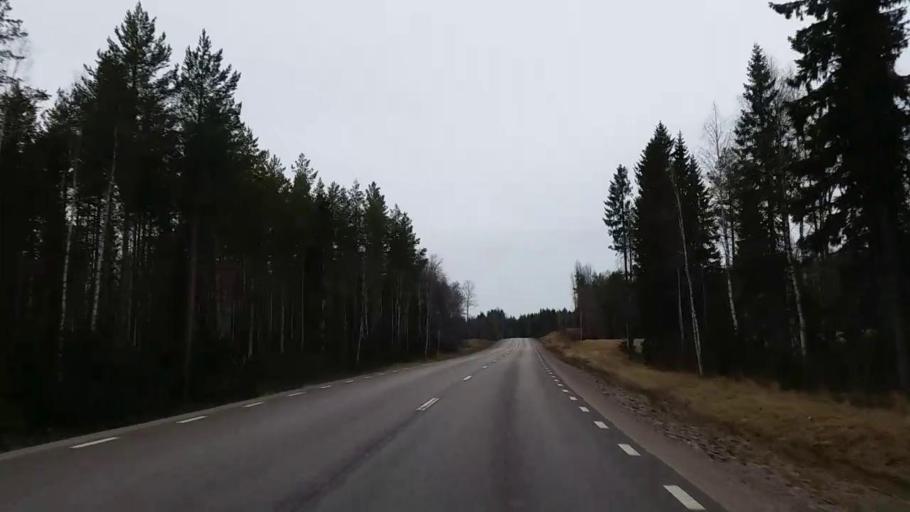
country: SE
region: Gaevleborg
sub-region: Ovanakers Kommun
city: Edsbyn
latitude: 61.1963
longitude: 15.8738
